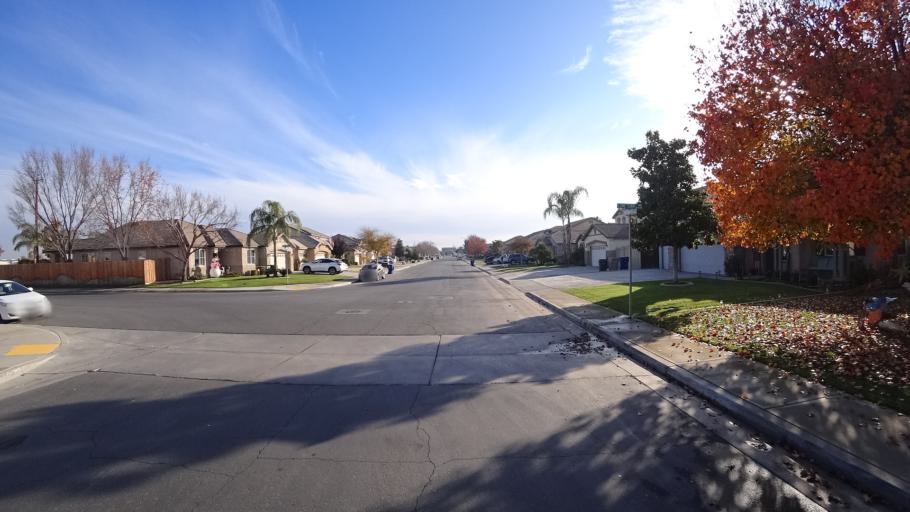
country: US
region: California
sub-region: Kern County
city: Rosedale
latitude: 35.4118
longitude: -119.1414
